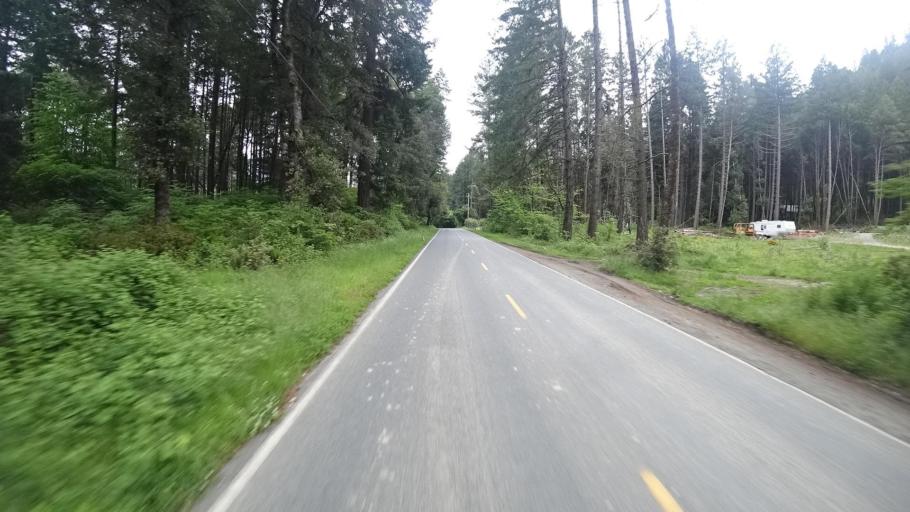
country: US
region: California
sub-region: Humboldt County
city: Willow Creek
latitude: 41.0833
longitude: -123.7038
